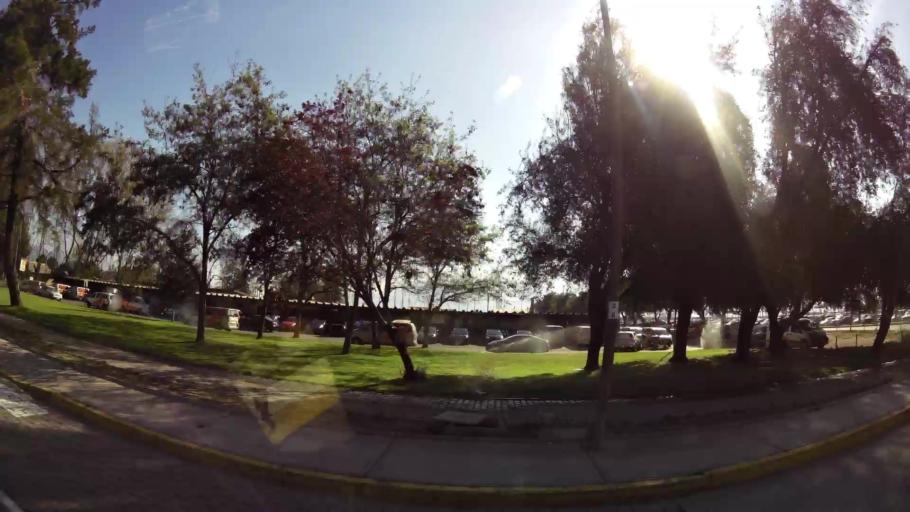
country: CL
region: Santiago Metropolitan
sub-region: Provincia de Santiago
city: Lo Prado
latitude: -33.4026
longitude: -70.7920
